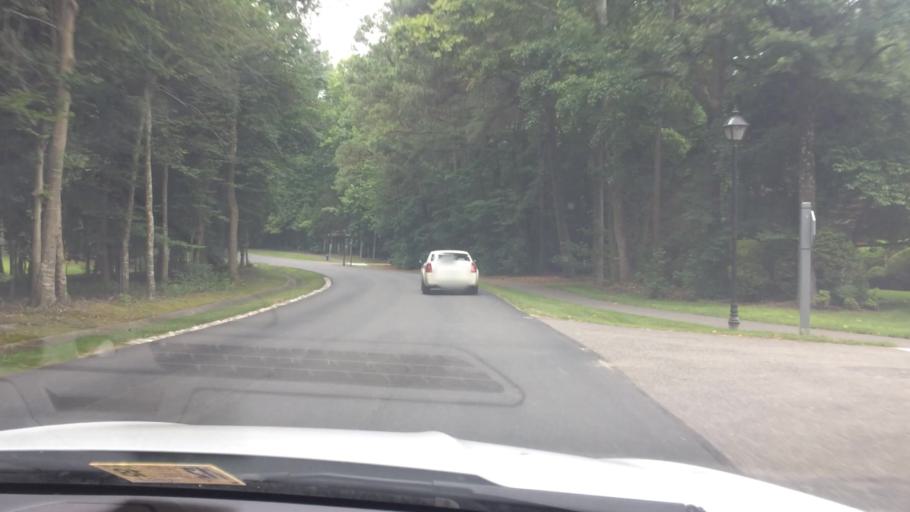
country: US
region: Virginia
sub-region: James City County
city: Williamsburg
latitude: 37.2988
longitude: -76.7756
